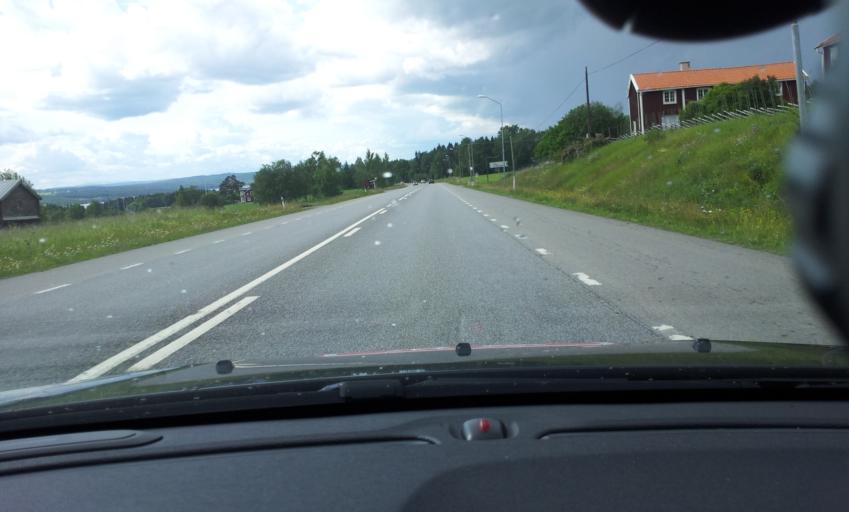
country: SE
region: Jaemtland
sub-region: Krokoms Kommun
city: Krokom
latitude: 63.3162
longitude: 14.0927
